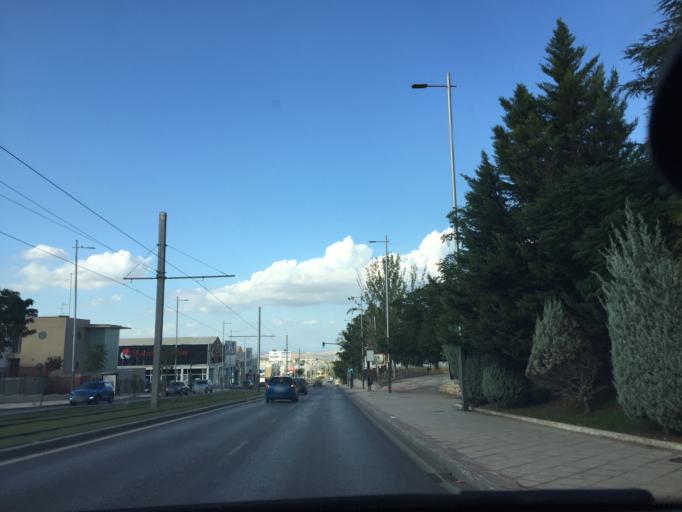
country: ES
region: Andalusia
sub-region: Provincia de Jaen
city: Jaen
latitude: 37.7855
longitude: -3.7833
